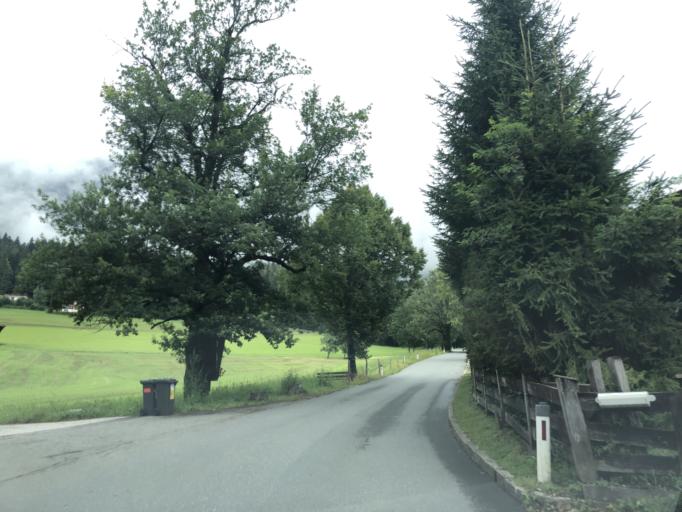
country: AT
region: Tyrol
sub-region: Politischer Bezirk Kufstein
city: Scheffau am Wilden Kaiser
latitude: 47.5320
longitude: 12.2449
